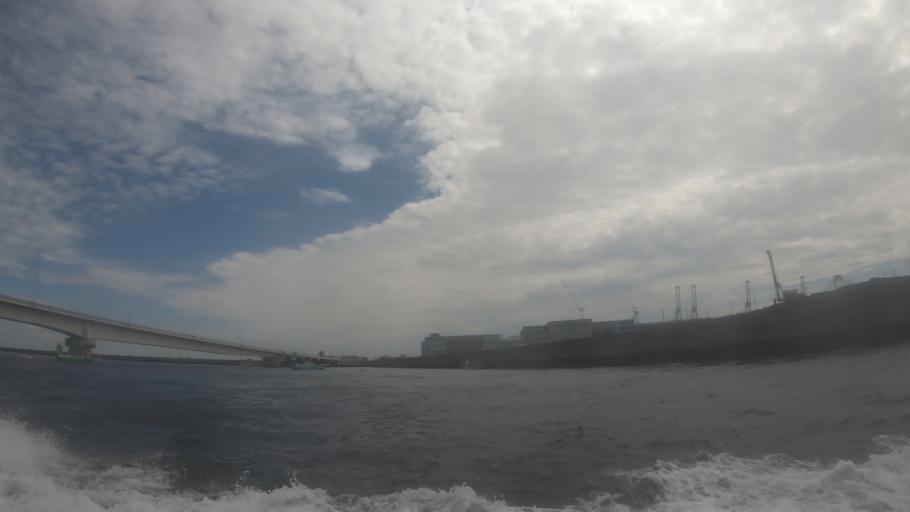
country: JP
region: Kanagawa
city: Yokohama
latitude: 35.4105
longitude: 139.6799
